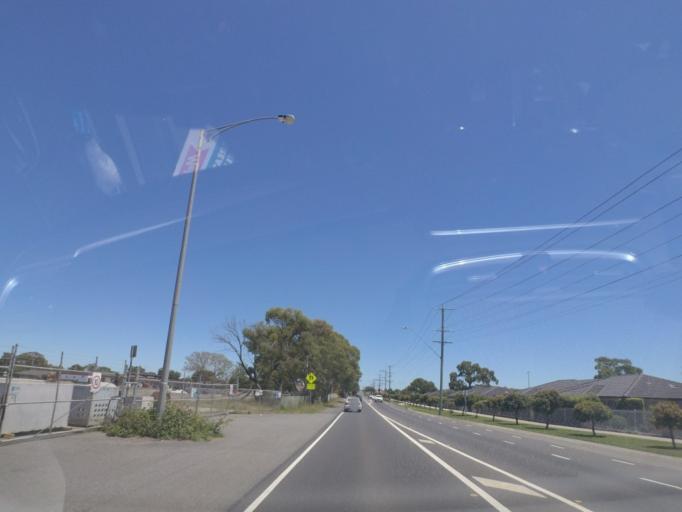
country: AU
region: Victoria
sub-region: Whittlesea
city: Mill Park
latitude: -37.6485
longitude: 145.0630
